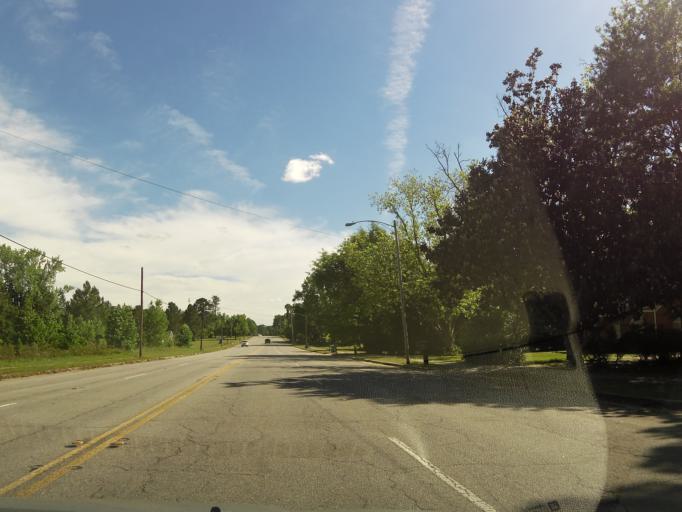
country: US
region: South Carolina
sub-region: Bamberg County
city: Denmark
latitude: 33.3046
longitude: -81.1451
